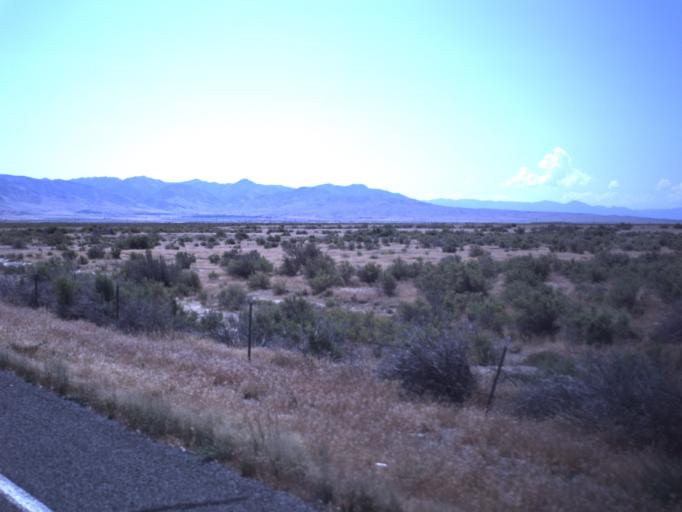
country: US
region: Utah
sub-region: Millard County
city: Delta
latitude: 39.4693
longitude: -112.4563
